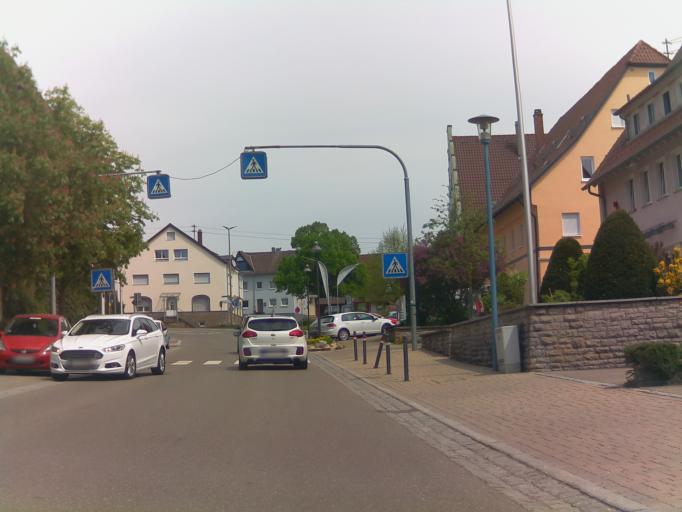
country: DE
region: Baden-Wuerttemberg
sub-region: Freiburg Region
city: Deisslingen
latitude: 48.1131
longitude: 8.6047
